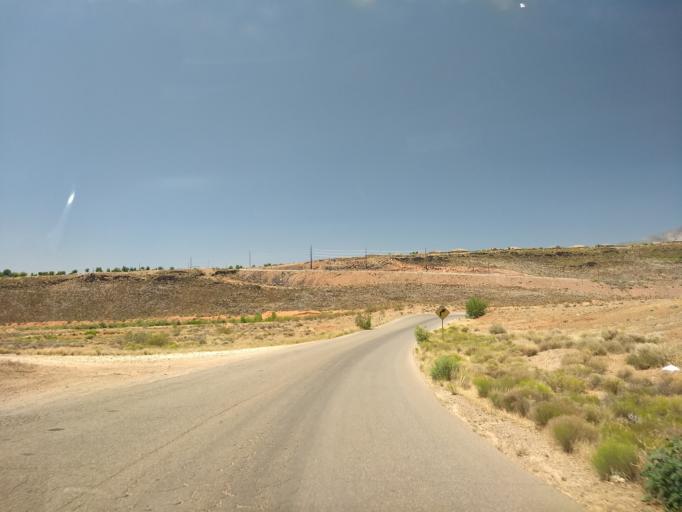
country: US
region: Utah
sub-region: Washington County
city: Washington
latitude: 37.1354
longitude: -113.4626
